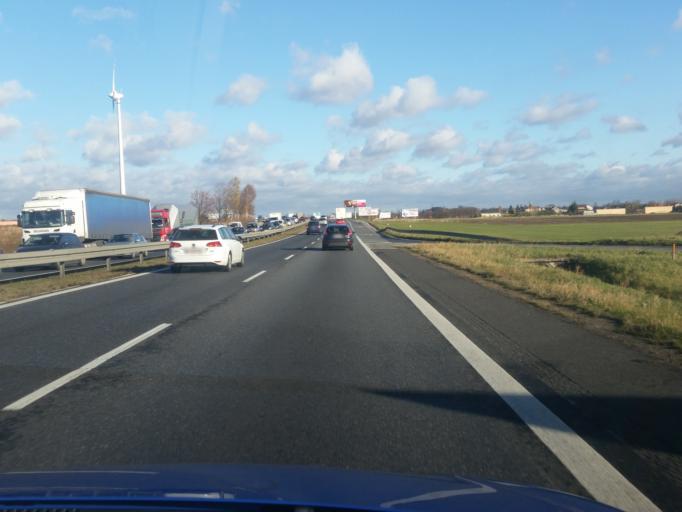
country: PL
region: Silesian Voivodeship
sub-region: Powiat czestochowski
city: Huta Stara B
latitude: 50.7212
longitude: 19.1568
